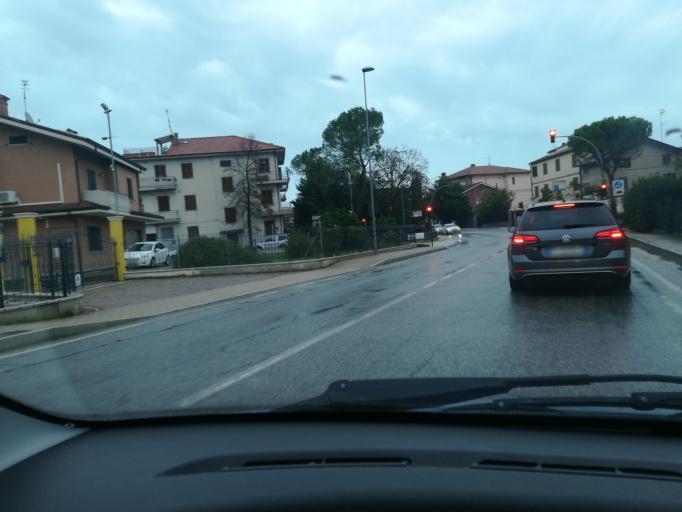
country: IT
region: The Marches
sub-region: Provincia di Macerata
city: Borgo Stazione
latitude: 43.2833
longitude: 13.6385
